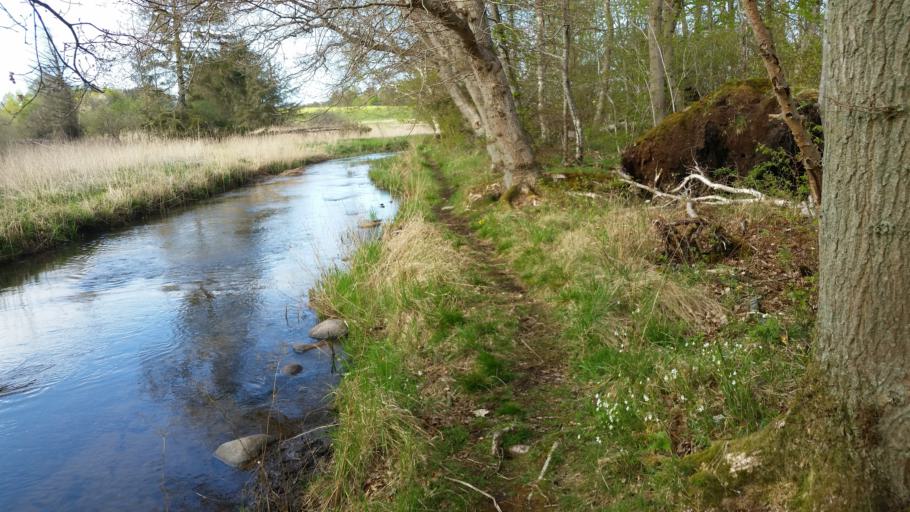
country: DK
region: Capital Region
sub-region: Gribskov Kommune
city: Gilleleje
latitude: 56.0701
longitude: 12.3636
